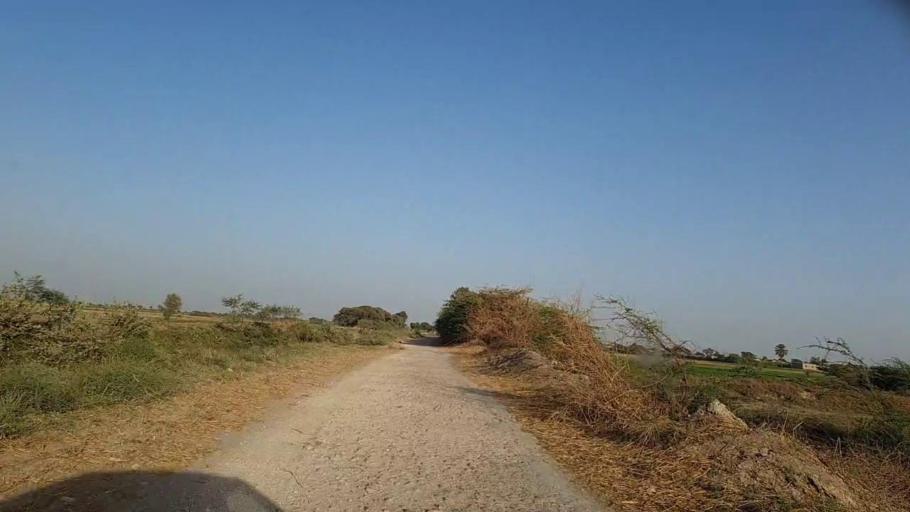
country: PK
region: Sindh
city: Jati
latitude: 24.4148
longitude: 68.3113
